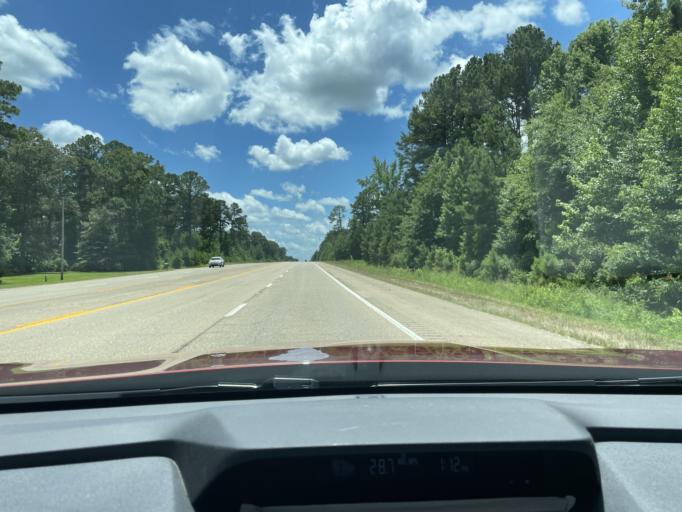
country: US
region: Arkansas
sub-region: Drew County
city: Monticello
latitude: 33.6934
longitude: -91.8064
